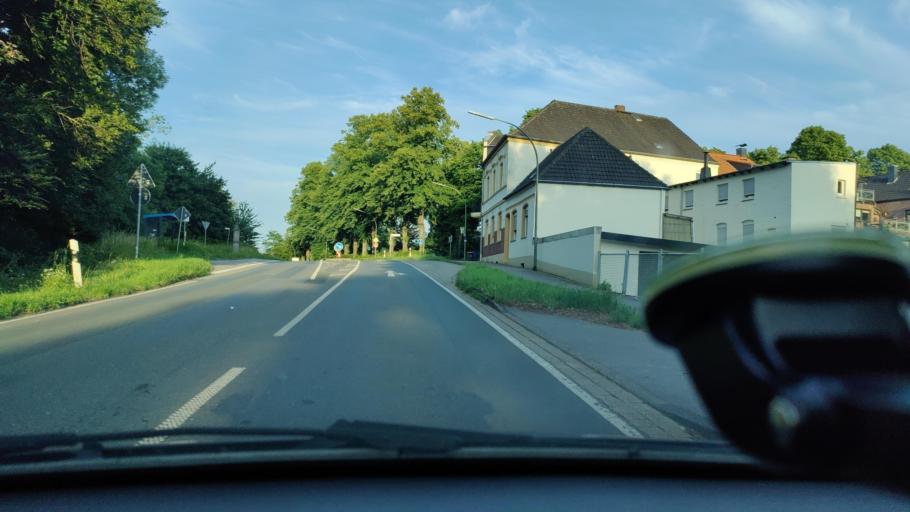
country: DE
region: North Rhine-Westphalia
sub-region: Regierungsbezirk Dusseldorf
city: Kamp-Lintfort
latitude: 51.5055
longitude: 6.5150
